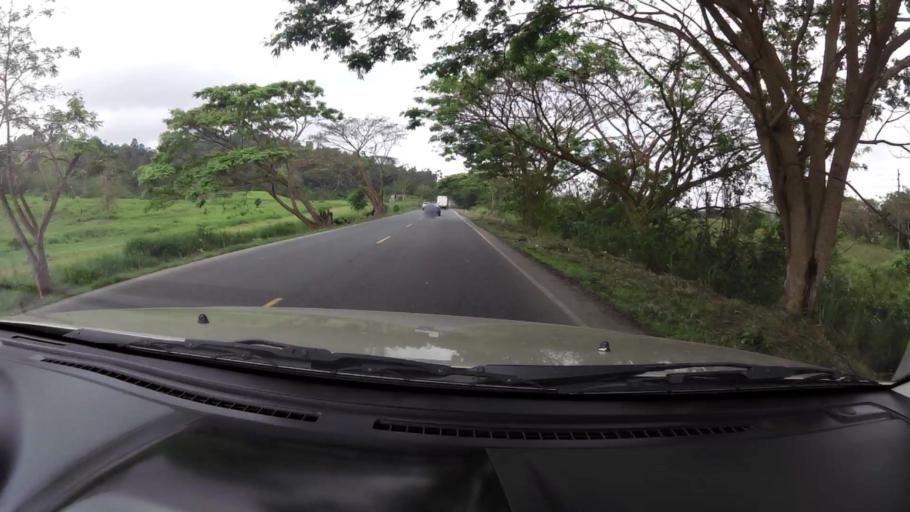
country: EC
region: Guayas
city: Naranjal
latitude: -2.7788
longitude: -79.6981
